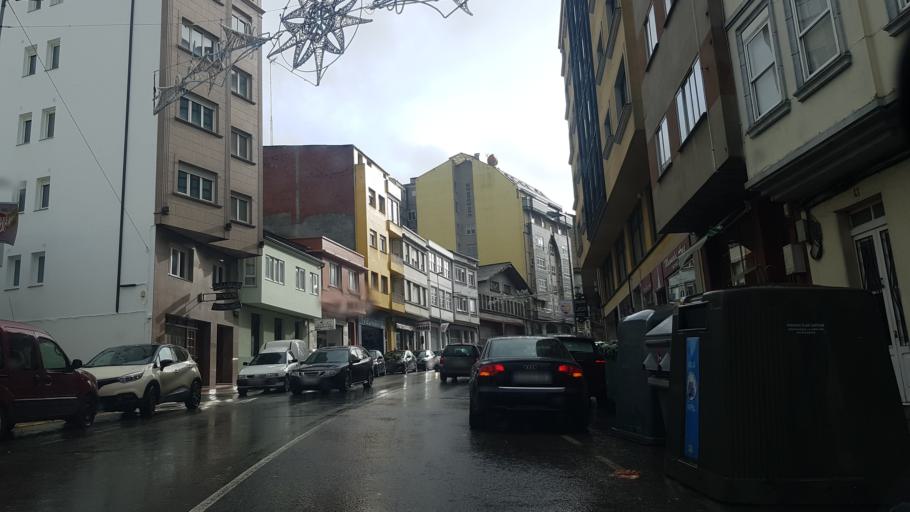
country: ES
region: Galicia
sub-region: Provincia de Lugo
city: Vilalba
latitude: 43.3012
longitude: -7.6791
